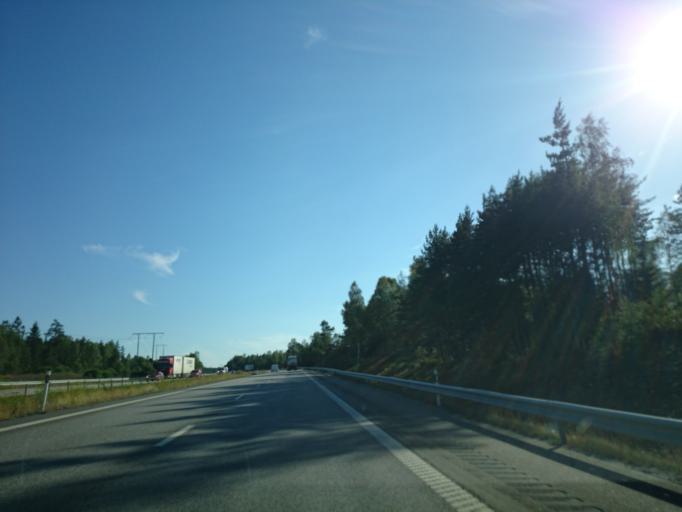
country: SE
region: Soedermanland
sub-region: Oxelosunds Kommun
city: Oxelosund
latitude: 58.8349
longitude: 17.1713
